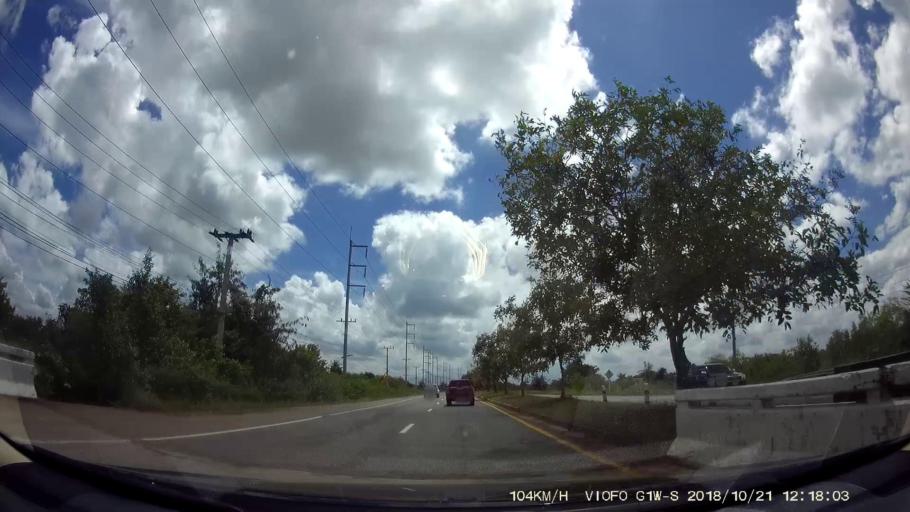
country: TH
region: Nakhon Ratchasima
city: Dan Khun Thot
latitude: 15.3226
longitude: 101.8179
